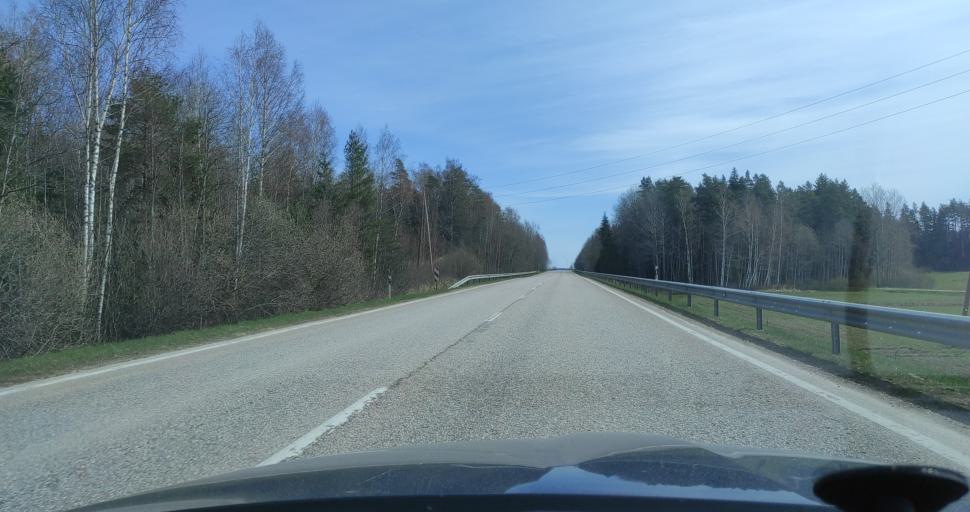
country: LV
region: Talsu Rajons
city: Stende
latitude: 57.2052
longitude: 22.4440
